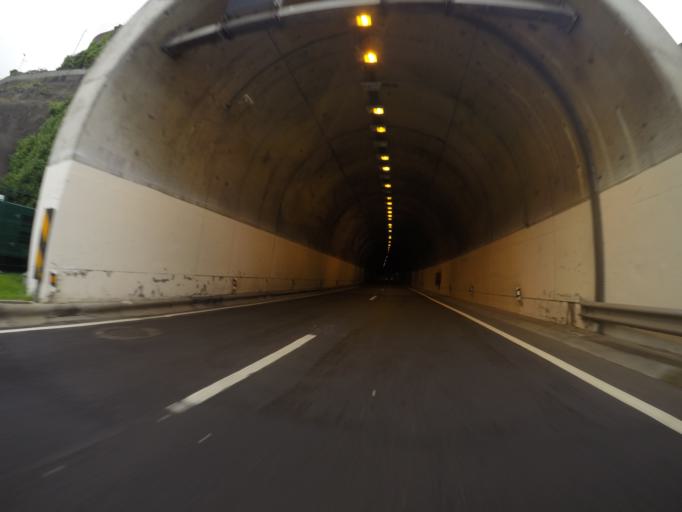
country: PT
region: Madeira
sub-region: Funchal
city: Nossa Senhora do Monte
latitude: 32.6618
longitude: -16.9187
